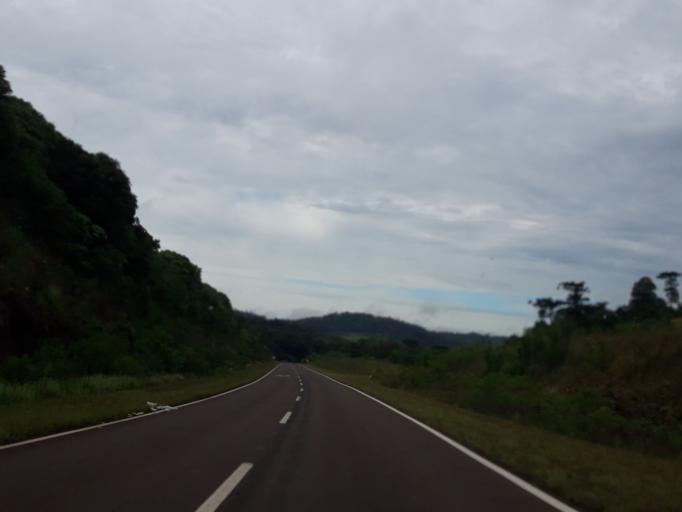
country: AR
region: Misiones
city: Bernardo de Irigoyen
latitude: -26.3249
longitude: -53.7569
